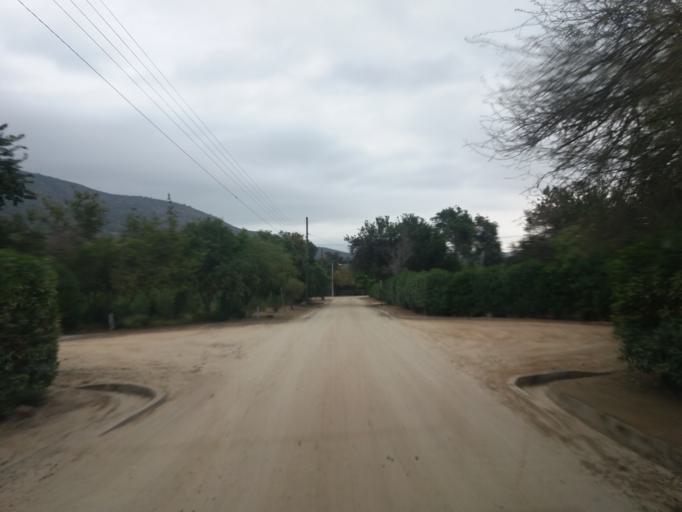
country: CL
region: Valparaiso
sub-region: Provincia de Marga Marga
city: Limache
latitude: -33.0267
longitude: -71.1379
